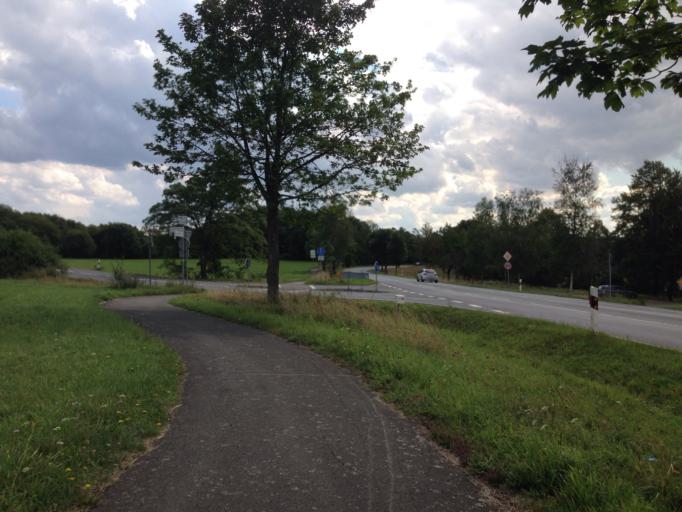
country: DE
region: Hesse
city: Mengerskirchen
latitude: 50.5480
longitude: 8.1531
